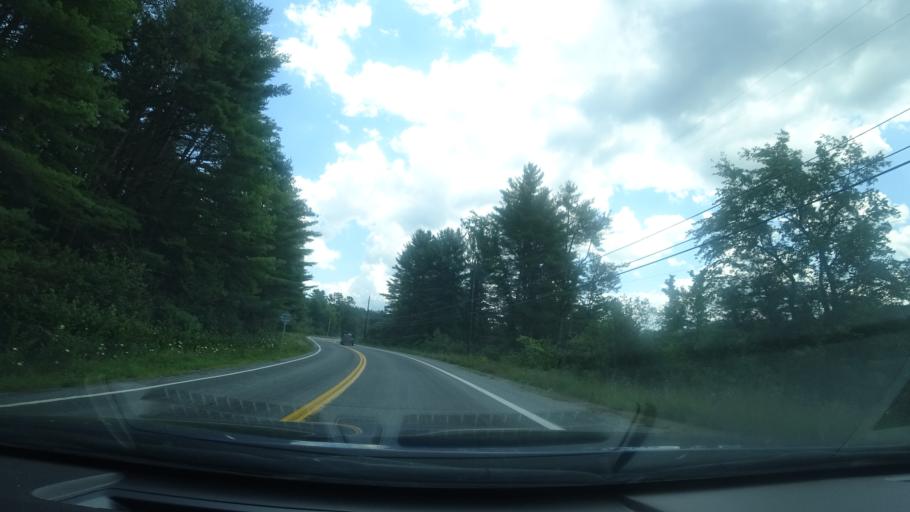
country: US
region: New York
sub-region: Warren County
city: Warrensburg
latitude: 43.6613
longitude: -73.8205
